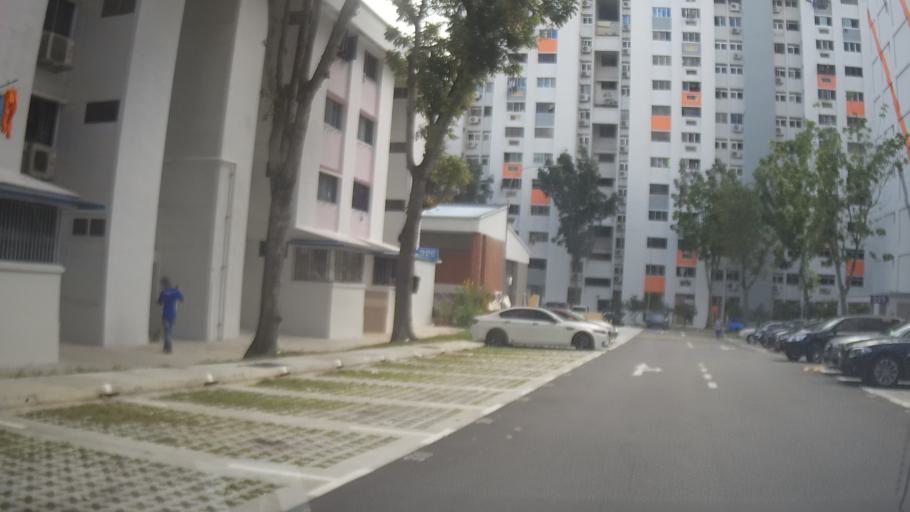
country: MY
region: Johor
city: Johor Bahru
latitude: 1.4302
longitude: 103.7789
